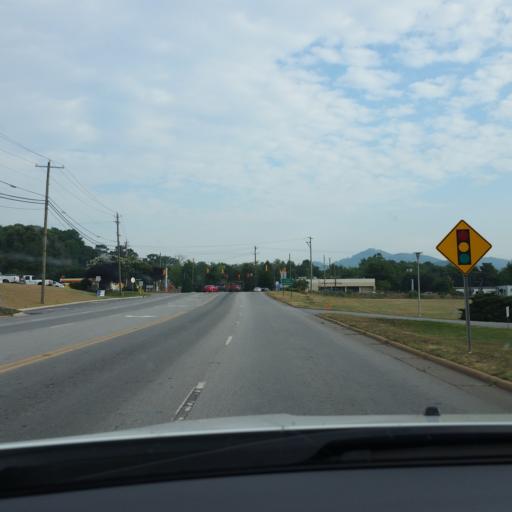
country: US
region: North Carolina
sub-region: Buncombe County
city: Bent Creek
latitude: 35.5437
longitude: -82.6577
